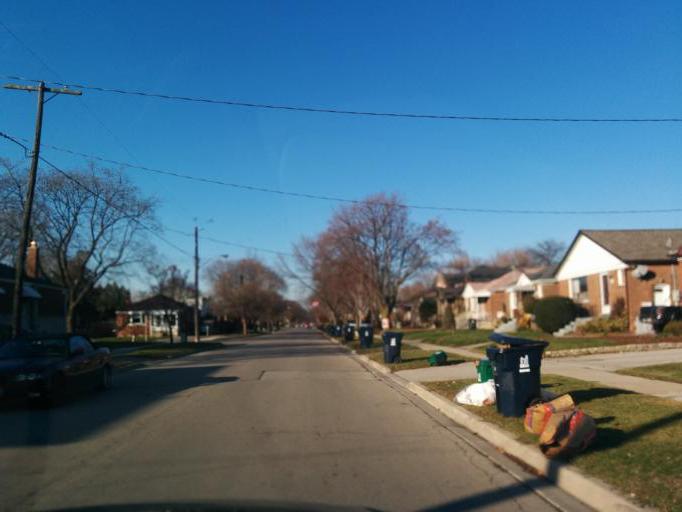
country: CA
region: Ontario
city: Etobicoke
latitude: 43.6046
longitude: -79.5338
